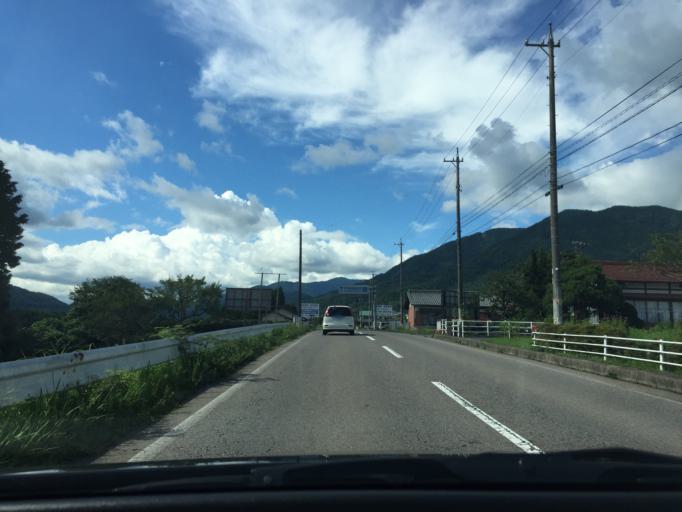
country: JP
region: Gifu
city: Nakatsugawa
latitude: 35.6501
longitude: 137.4360
